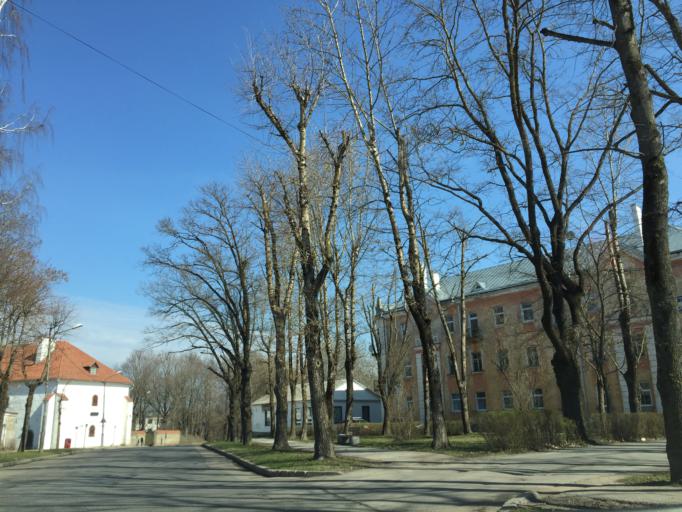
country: EE
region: Ida-Virumaa
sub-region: Narva linn
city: Narva
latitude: 59.3815
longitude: 28.1965
